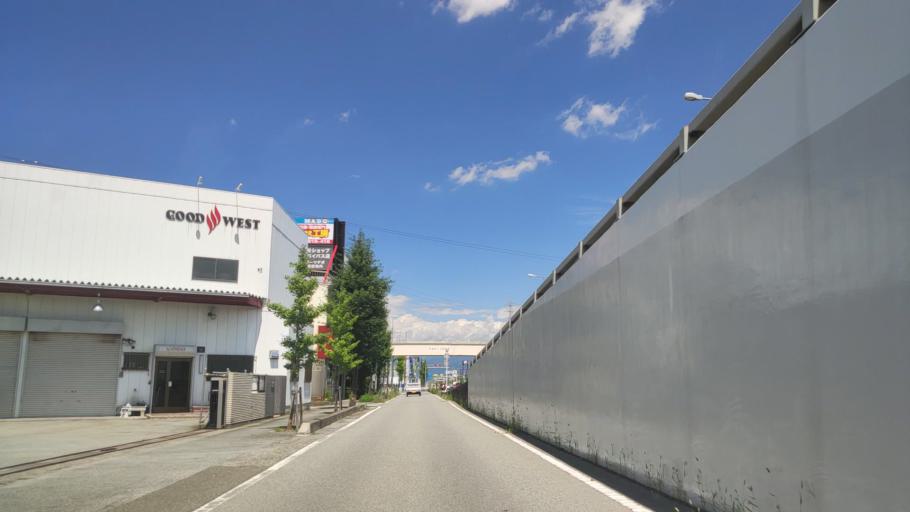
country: JP
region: Yamanashi
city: Kofu-shi
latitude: 35.6347
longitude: 138.5782
